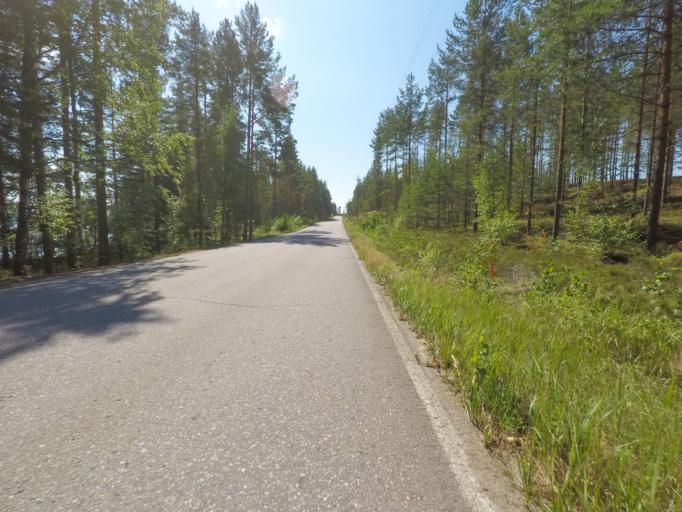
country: FI
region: Southern Savonia
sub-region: Mikkeli
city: Puumala
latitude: 61.4583
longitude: 28.1748
